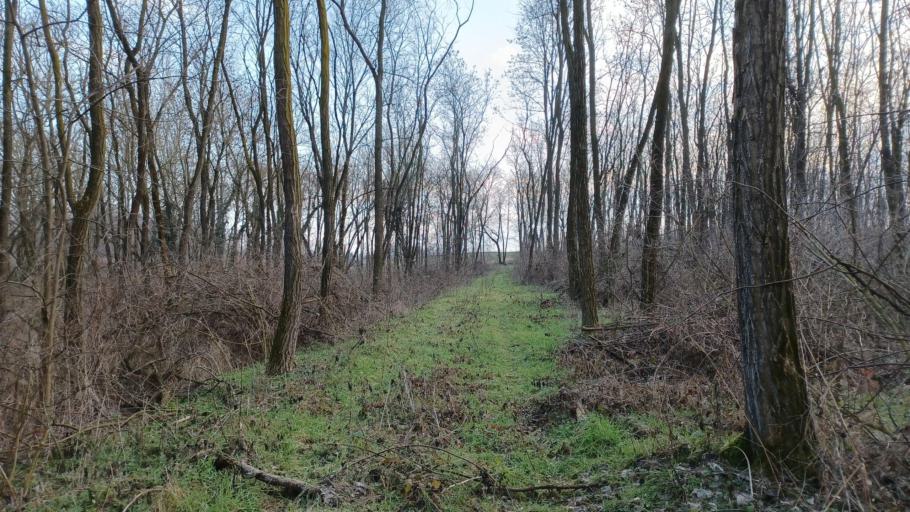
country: HU
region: Tolna
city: Tengelic
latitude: 46.5314
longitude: 18.7017
